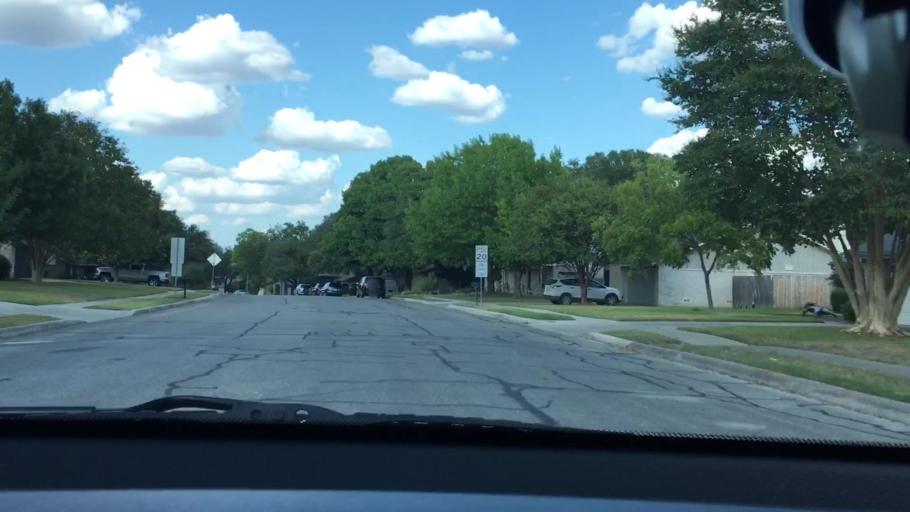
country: US
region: Texas
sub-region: Bexar County
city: Selma
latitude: 29.5688
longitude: -98.3162
